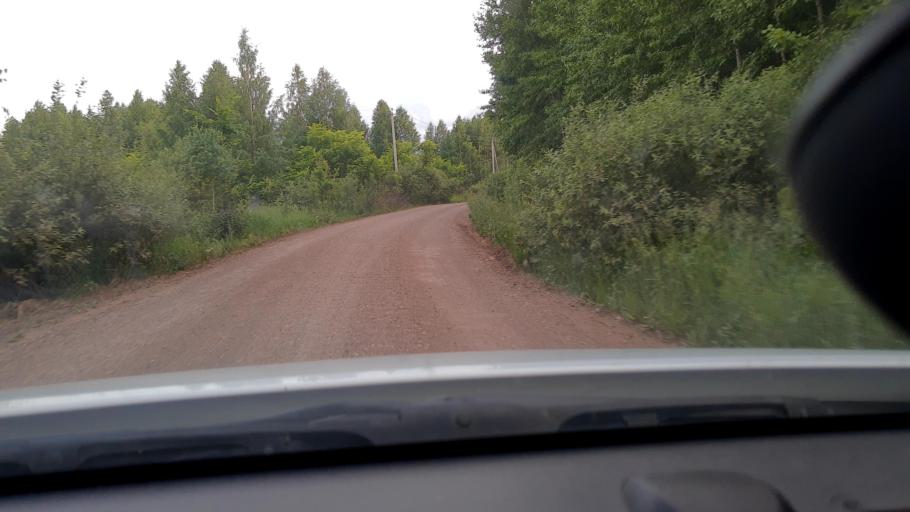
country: RU
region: Bashkortostan
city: Kabakovo
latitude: 54.4439
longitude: 55.9146
